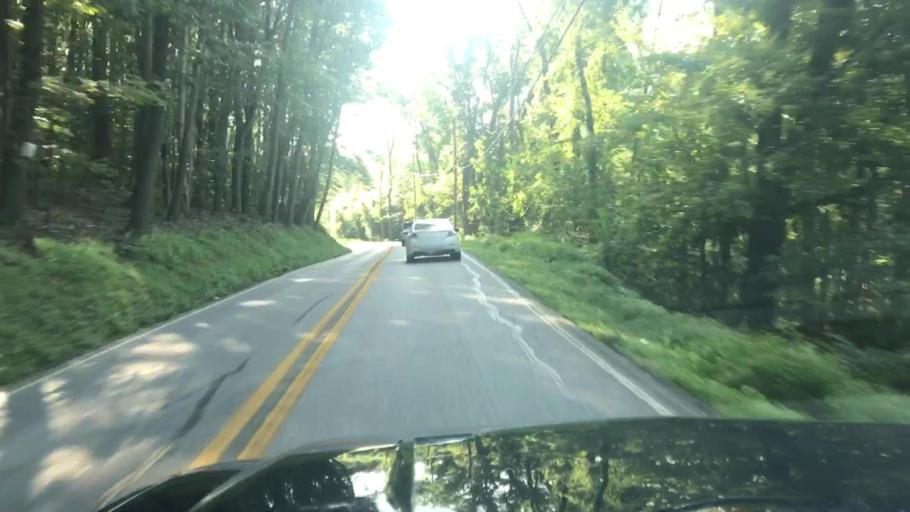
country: US
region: Pennsylvania
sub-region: York County
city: Valley Green
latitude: 40.1509
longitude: -76.8237
